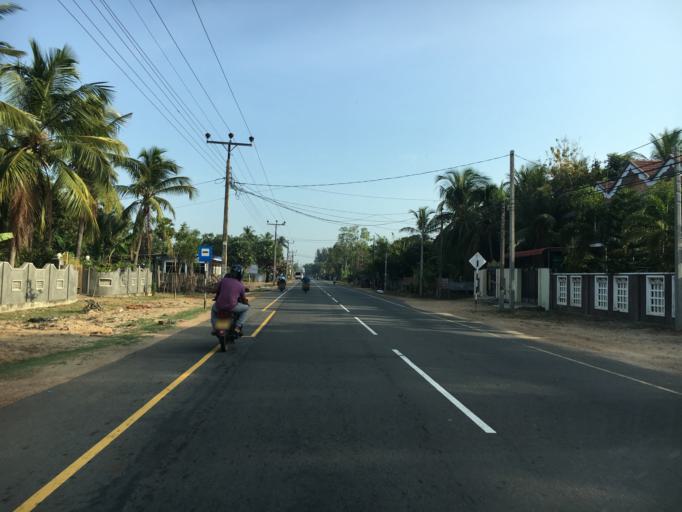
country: LK
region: Eastern Province
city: Eravur Town
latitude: 7.9003
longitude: 81.5356
